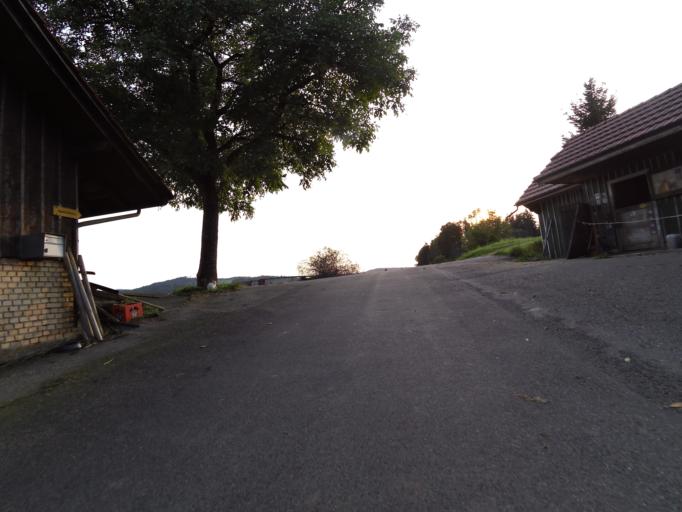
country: CH
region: Thurgau
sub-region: Frauenfeld District
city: Frauenfeld
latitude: 47.5263
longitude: 8.8974
